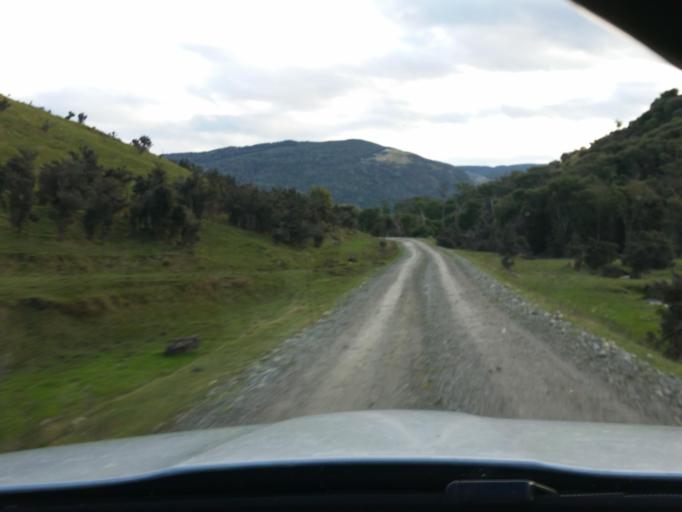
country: NZ
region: Southland
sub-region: Southland District
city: Te Anau
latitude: -45.8424
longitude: 167.6696
